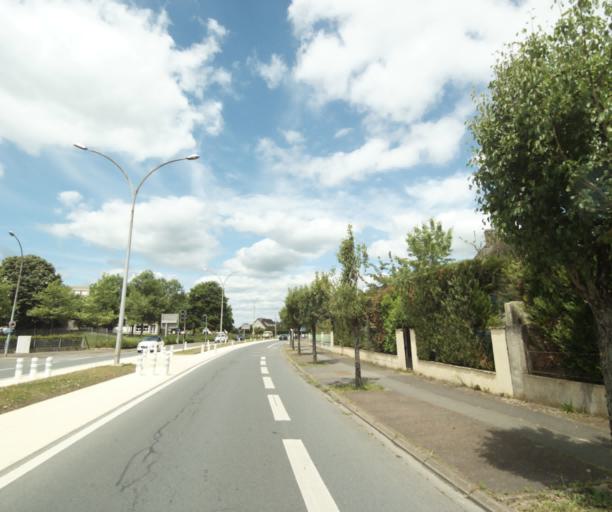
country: FR
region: Centre
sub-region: Departement d'Eure-et-Loir
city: Mainvilliers
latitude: 48.4383
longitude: 1.4506
